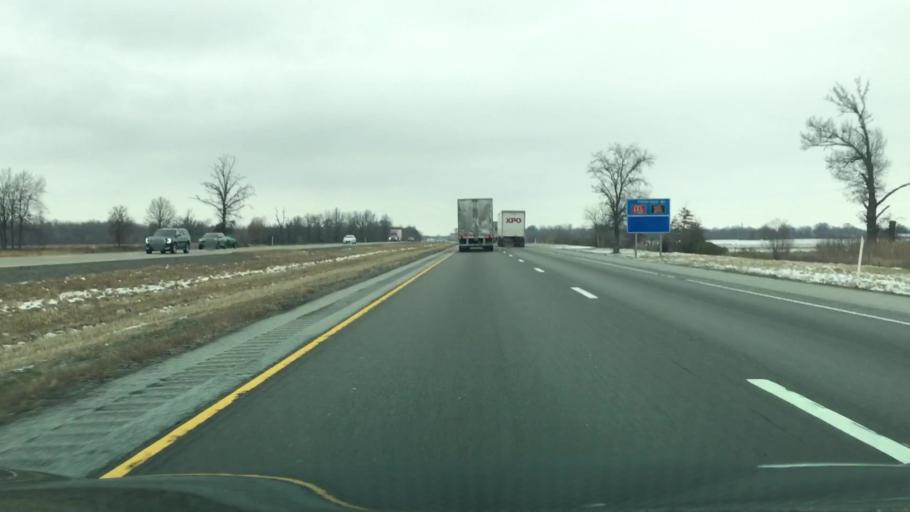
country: US
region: Illinois
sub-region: Jefferson County
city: Ina
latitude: 38.1321
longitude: -88.9119
